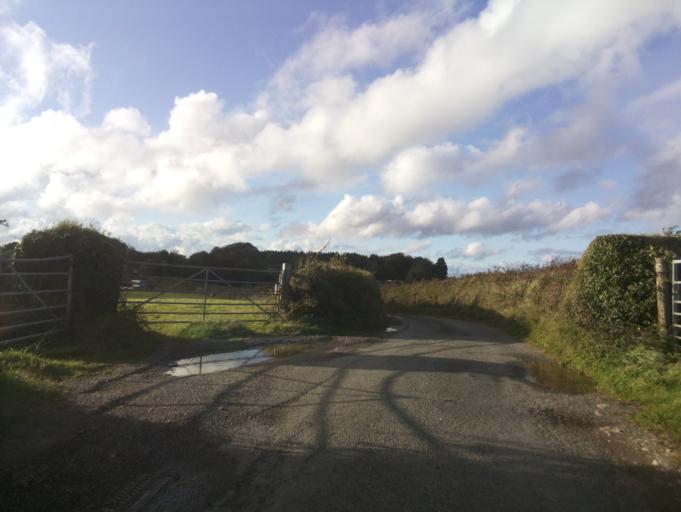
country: GB
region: England
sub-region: Devon
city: Dartmouth
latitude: 50.3463
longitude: -3.6116
